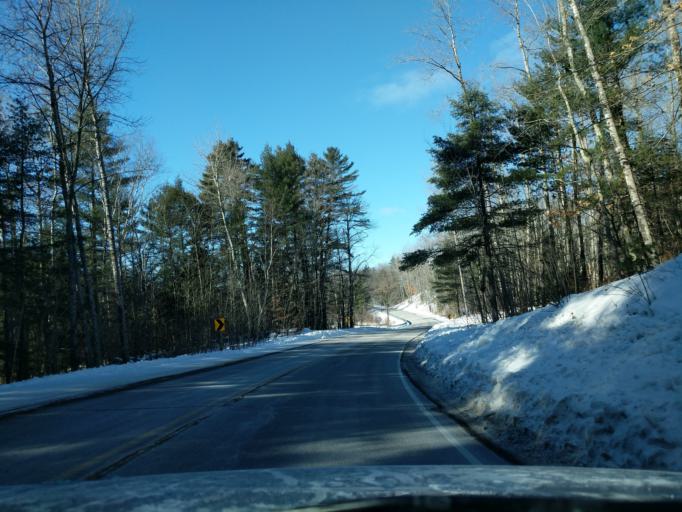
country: US
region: Wisconsin
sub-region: Menominee County
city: Keshena
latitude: 45.1137
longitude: -88.6471
